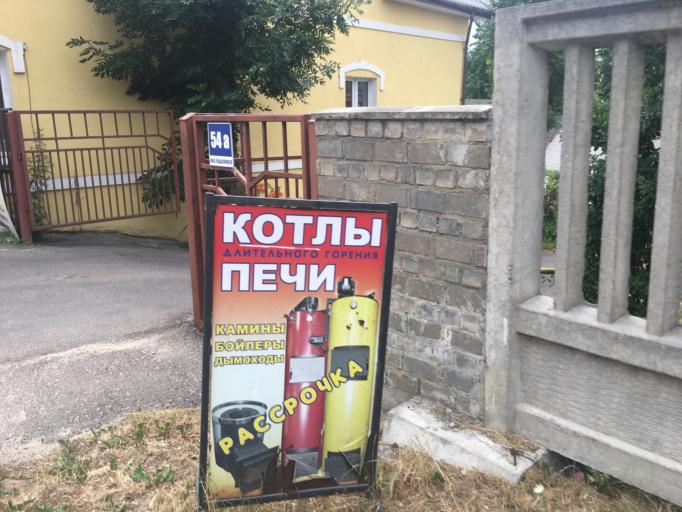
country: BY
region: Grodnenskaya
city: Hrodna
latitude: 53.6850
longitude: 23.8466
